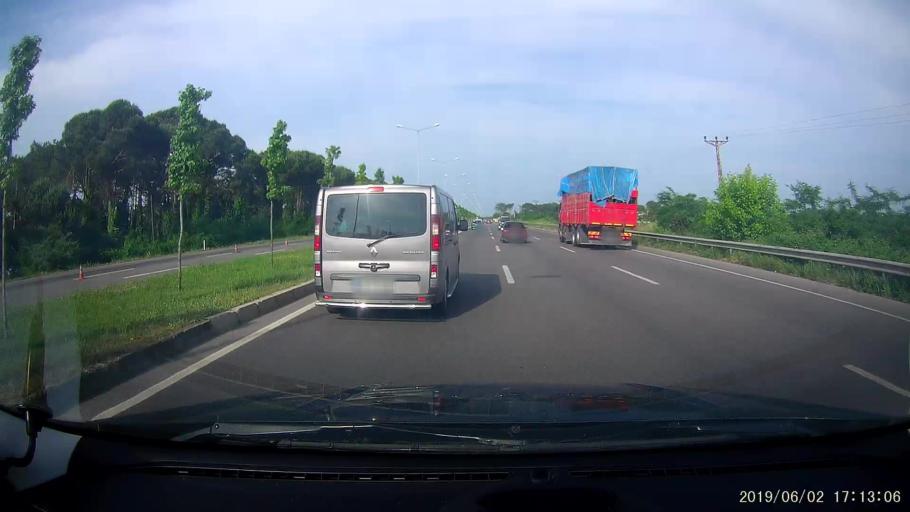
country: TR
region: Samsun
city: Tekkekoy
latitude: 41.2301
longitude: 36.5008
